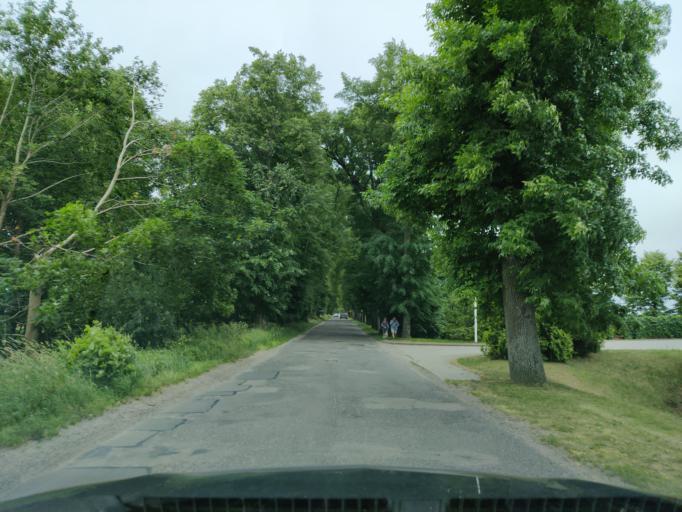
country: PL
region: Warmian-Masurian Voivodeship
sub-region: Powiat gizycki
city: Ryn
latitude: 53.9319
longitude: 21.5499
